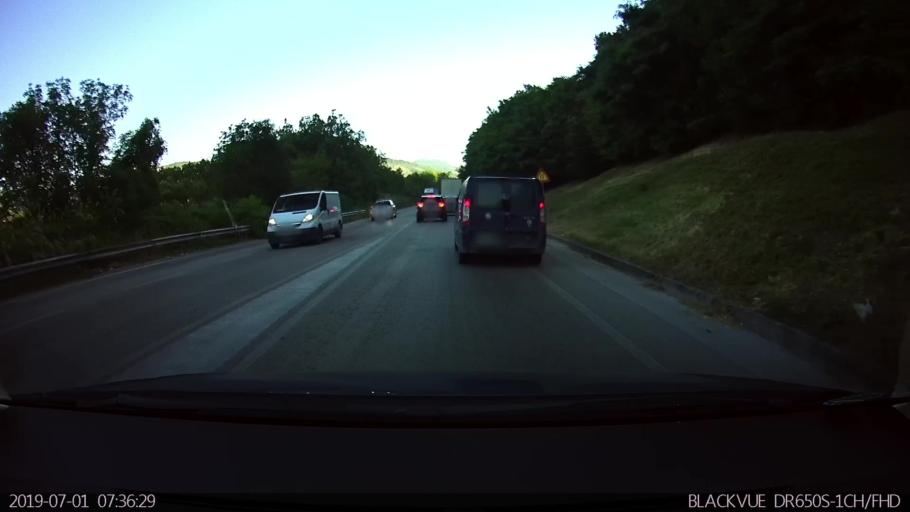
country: IT
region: Latium
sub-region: Provincia di Frosinone
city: Giuliano di Roma
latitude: 41.5320
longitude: 13.2670
